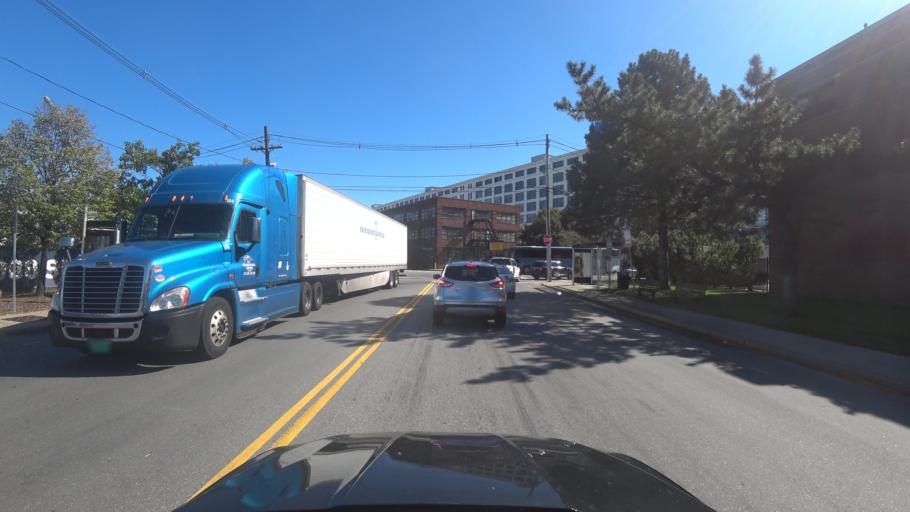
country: US
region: Massachusetts
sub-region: Suffolk County
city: South Boston
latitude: 42.3453
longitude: -71.0323
